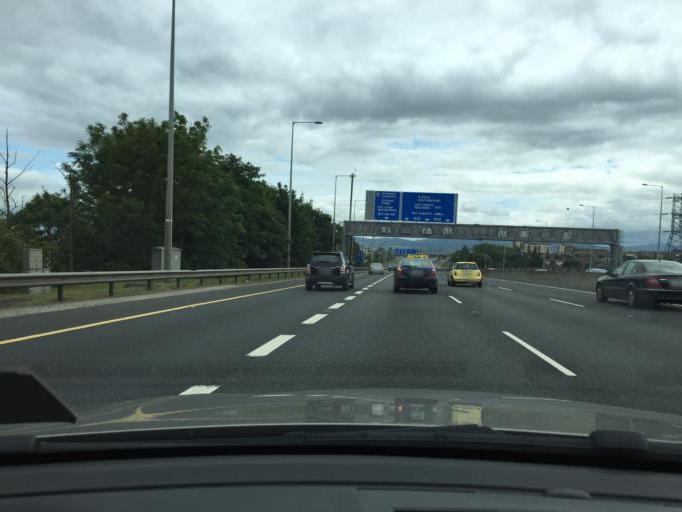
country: IE
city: Cherry Orchard
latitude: 53.3275
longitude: -6.3764
